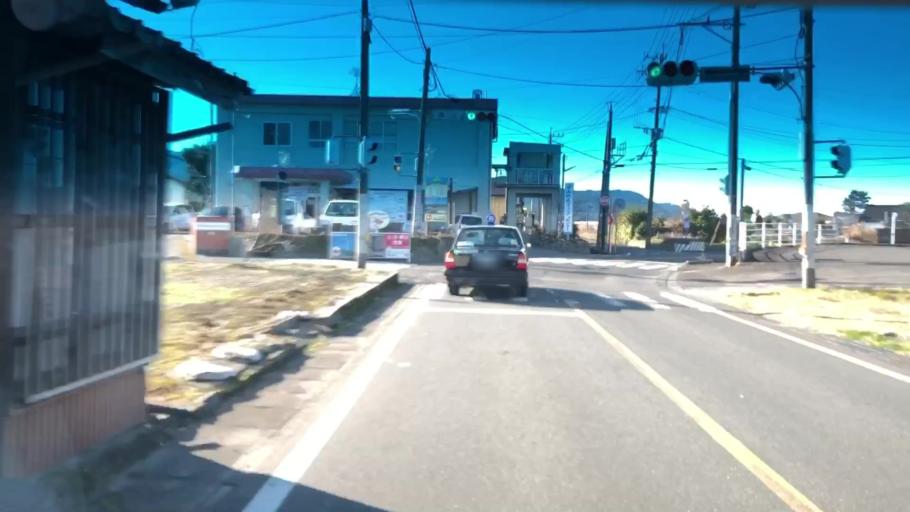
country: JP
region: Kagoshima
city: Satsumasendai
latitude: 31.8242
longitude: 130.2518
